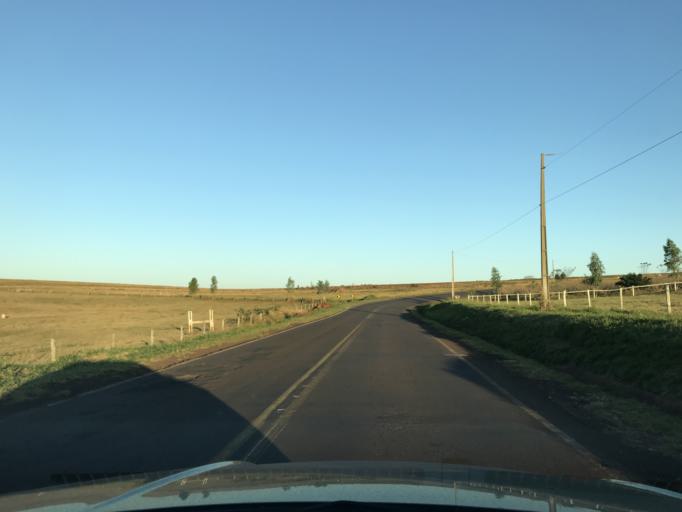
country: PY
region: Canindeyu
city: Salto del Guaira
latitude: -24.0852
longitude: -54.0918
